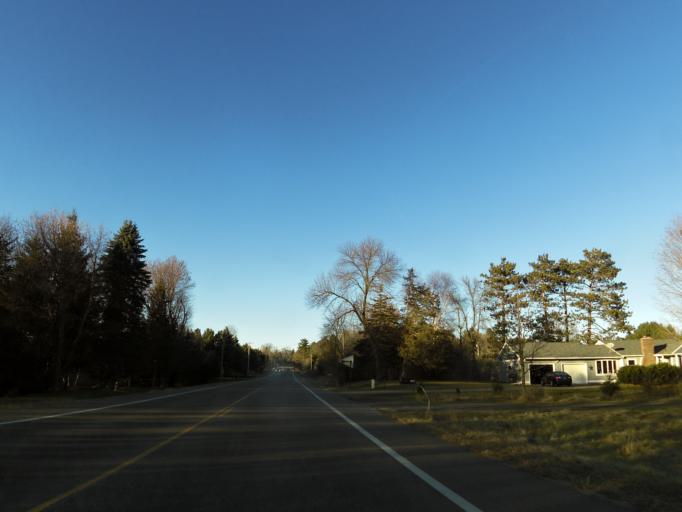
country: US
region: Minnesota
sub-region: Washington County
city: Stillwater
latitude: 45.0816
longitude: -92.8315
